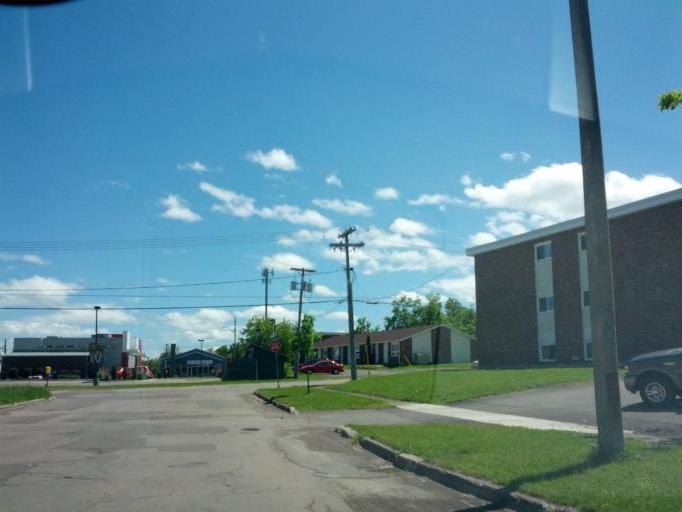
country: CA
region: New Brunswick
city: Moncton
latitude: 46.1138
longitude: -64.7780
